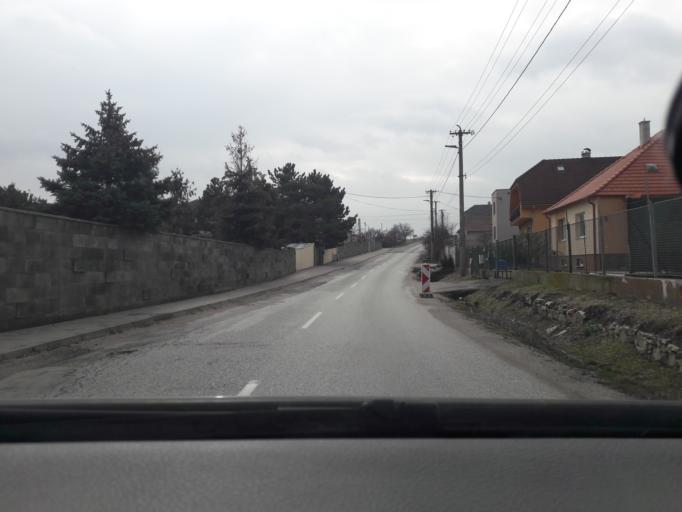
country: SK
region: Trnavsky
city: Smolenice
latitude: 48.4375
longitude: 17.4263
